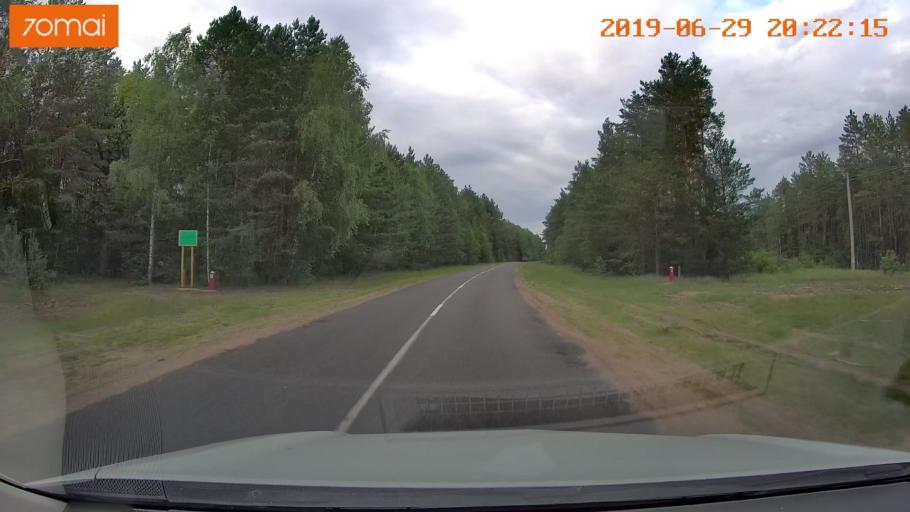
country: BY
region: Brest
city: Asnyezhytsy
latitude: 52.4296
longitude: 26.2538
